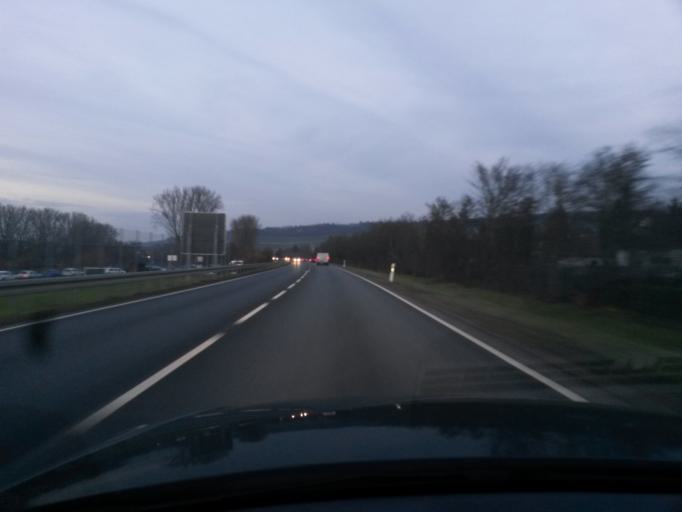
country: DE
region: Bavaria
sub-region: Regierungsbezirk Unterfranken
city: Sommerhausen
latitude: 49.7008
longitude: 10.0234
